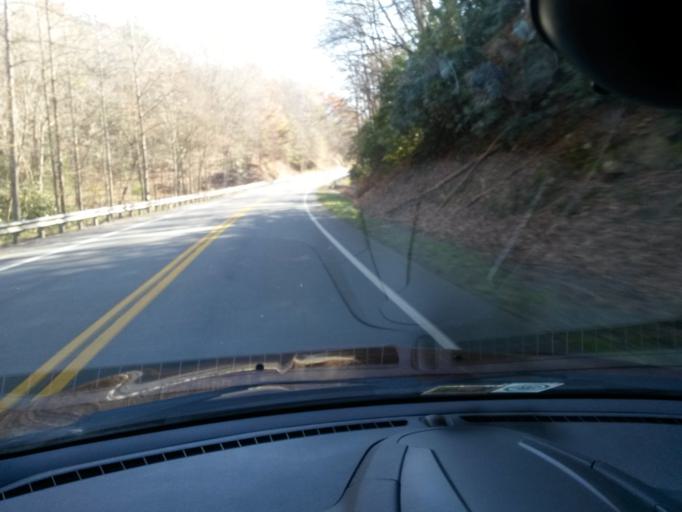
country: US
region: Virginia
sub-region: Henry County
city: Pannill Fork
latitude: 36.7724
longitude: -80.1075
